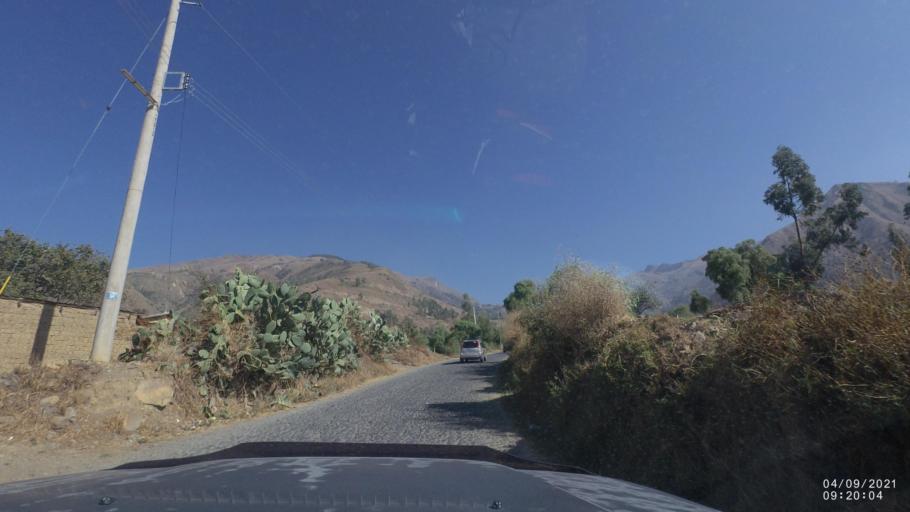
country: BO
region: Cochabamba
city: Sipe Sipe
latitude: -17.3651
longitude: -66.3611
